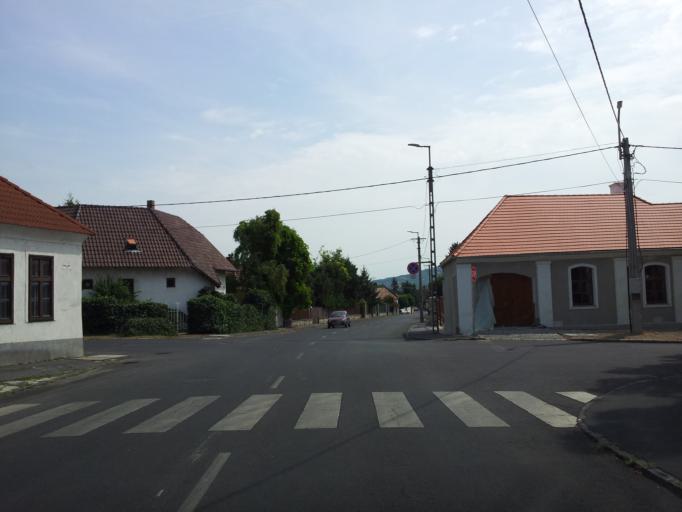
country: HU
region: Veszprem
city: Tapolca
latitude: 46.8809
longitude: 17.4428
